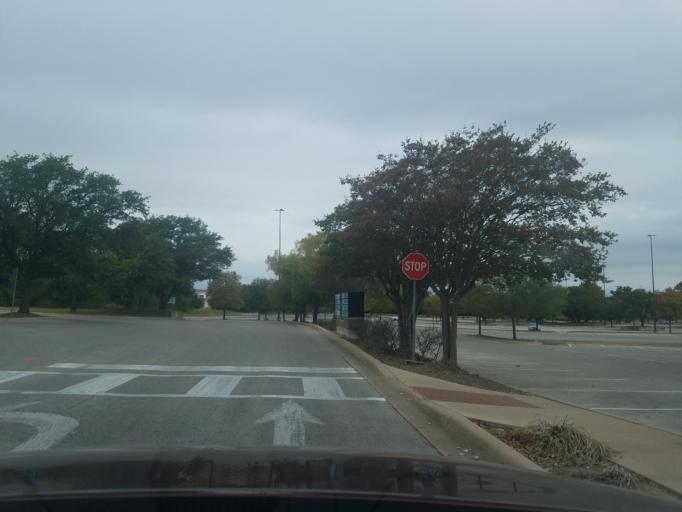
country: US
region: Texas
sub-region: Williamson County
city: Anderson Mill
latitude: 30.4676
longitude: -97.8087
